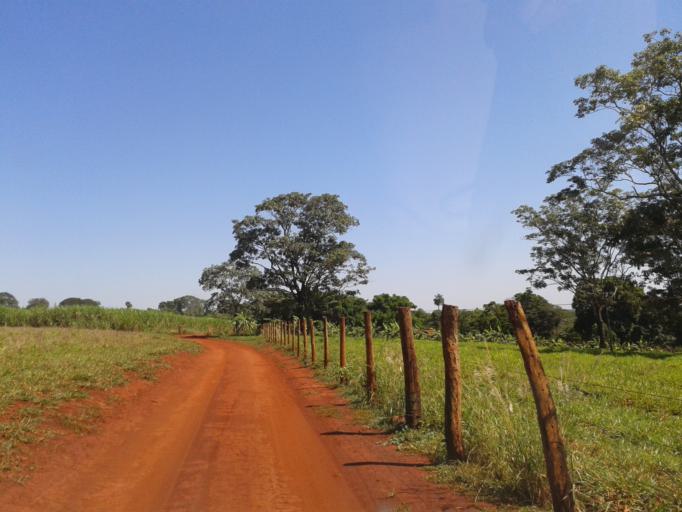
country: BR
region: Minas Gerais
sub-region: Centralina
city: Centralina
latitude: -18.6385
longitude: -49.2980
